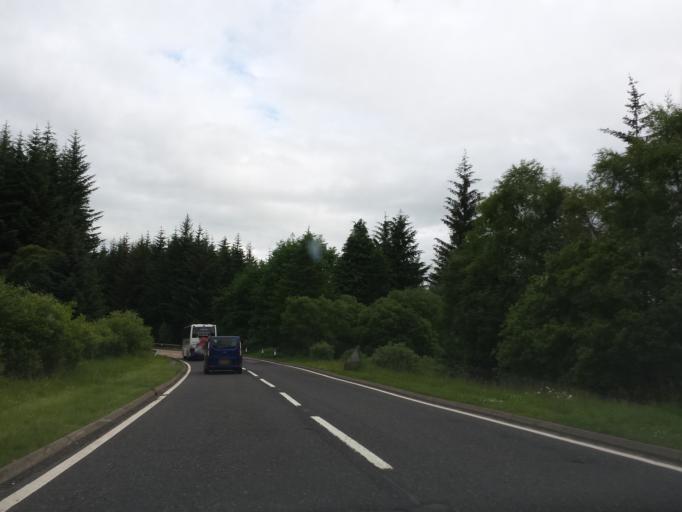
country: GB
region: Scotland
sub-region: Stirling
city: Callander
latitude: 56.4360
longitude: -4.3432
